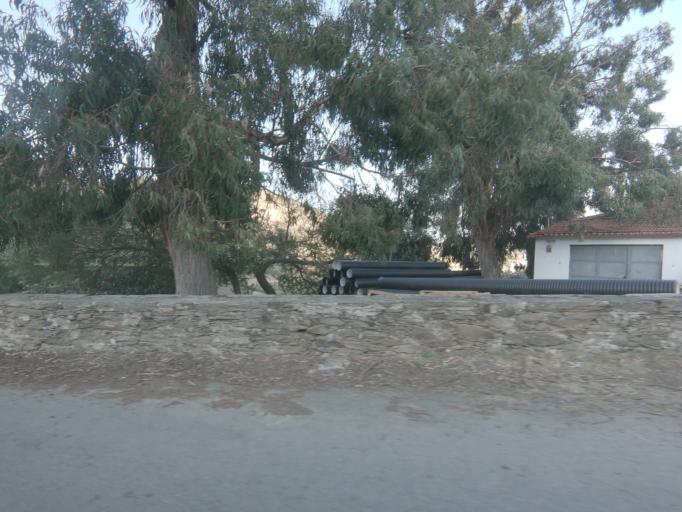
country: PT
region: Vila Real
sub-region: Sabrosa
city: Vilela
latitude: 41.1650
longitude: -7.6311
